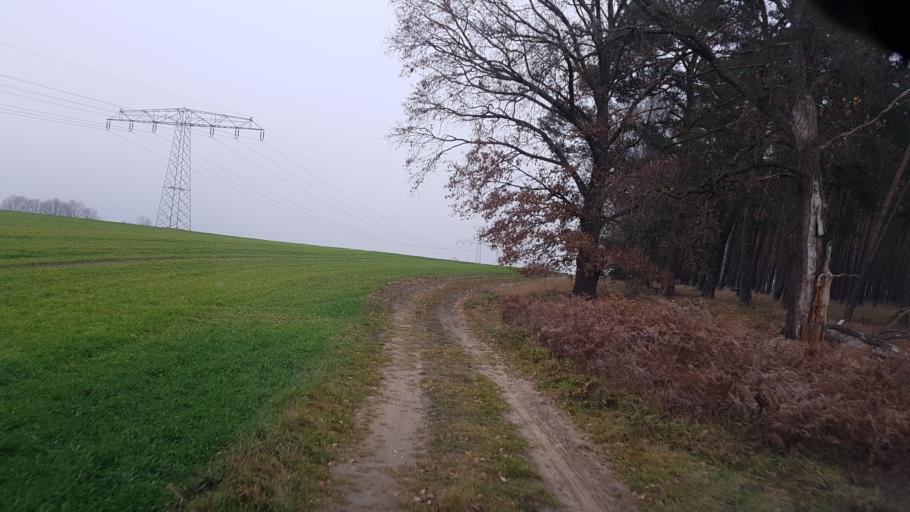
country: DE
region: Brandenburg
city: Altdobern
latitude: 51.6753
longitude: 13.9988
